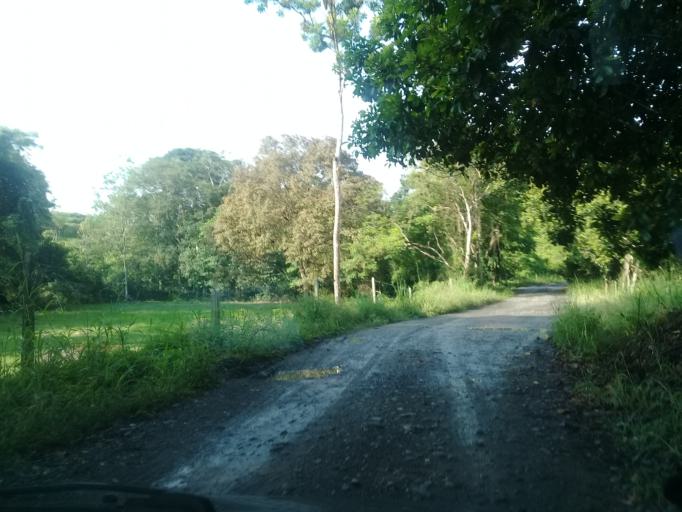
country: CO
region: Antioquia
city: Puerto Triunfo
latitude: 5.7386
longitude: -74.5009
